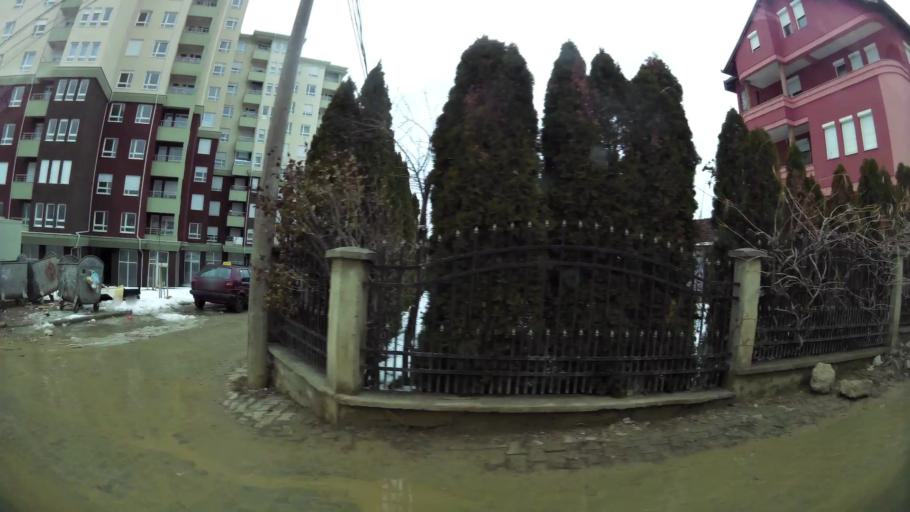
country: XK
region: Pristina
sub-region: Komuna e Prishtines
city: Pristina
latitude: 42.6552
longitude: 21.1854
